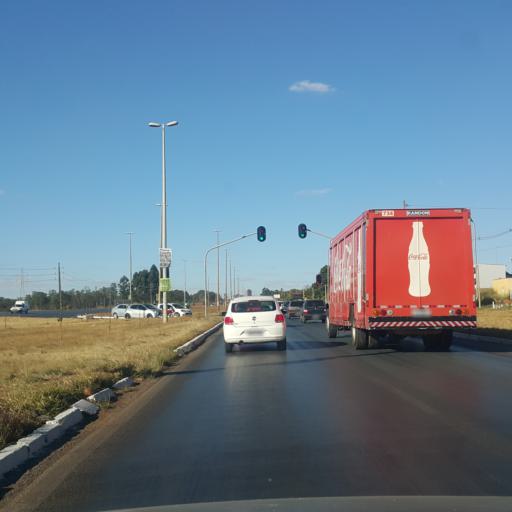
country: BR
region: Federal District
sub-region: Brasilia
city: Brasilia
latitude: -15.7973
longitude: -48.0702
